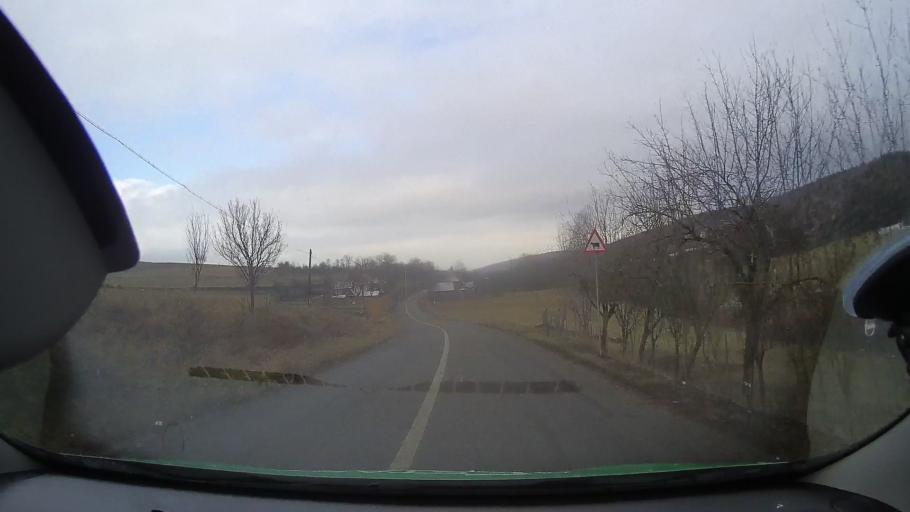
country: RO
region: Alba
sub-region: Comuna Farau
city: Farau
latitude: 46.3896
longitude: 24.0310
